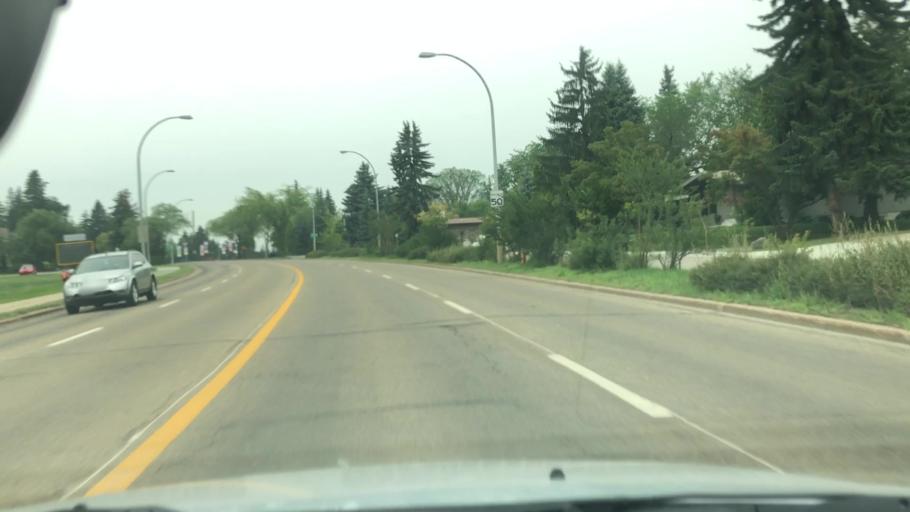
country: CA
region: Alberta
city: Edmonton
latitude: 53.5205
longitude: -113.5386
